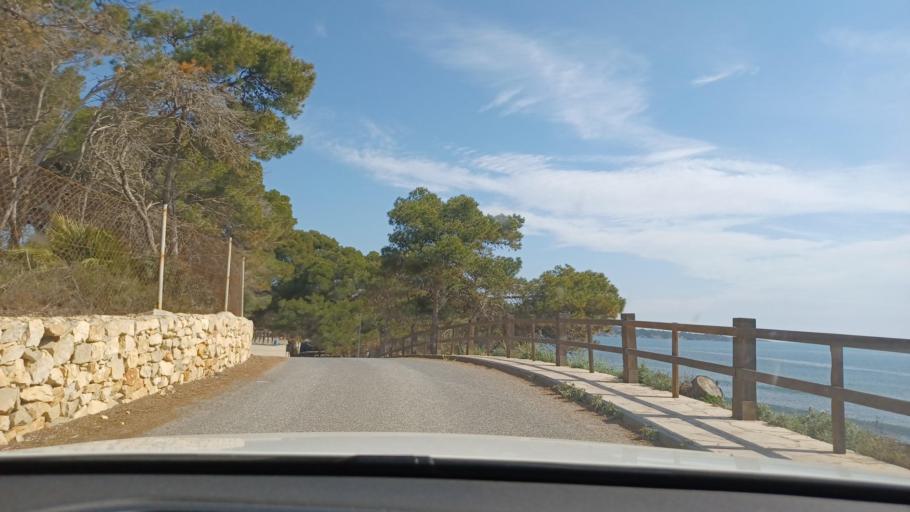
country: ES
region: Catalonia
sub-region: Provincia de Tarragona
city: L'Ampolla
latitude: 40.8296
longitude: 0.7412
